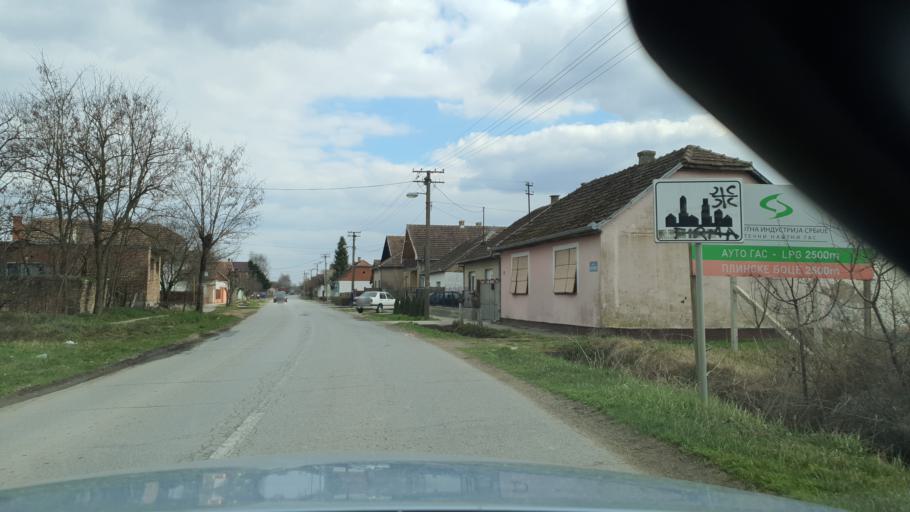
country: RS
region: Autonomna Pokrajina Vojvodina
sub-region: Juznobacki Okrug
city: Bac
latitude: 45.3886
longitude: 19.2214
